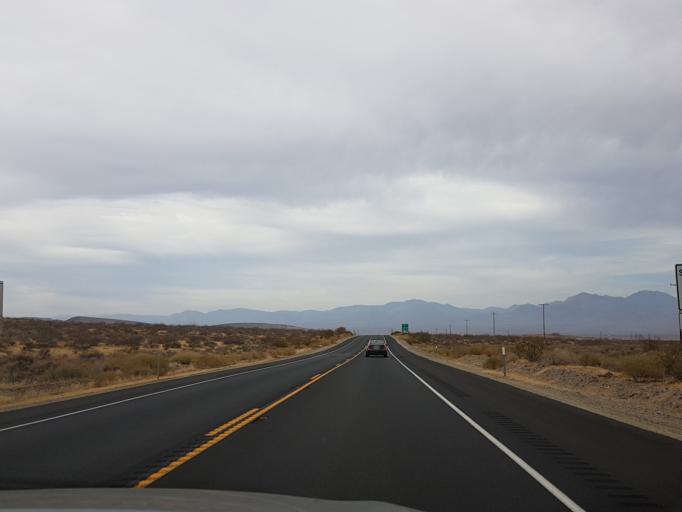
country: US
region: California
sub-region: Kern County
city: Ridgecrest
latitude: 35.5471
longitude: -117.7028
